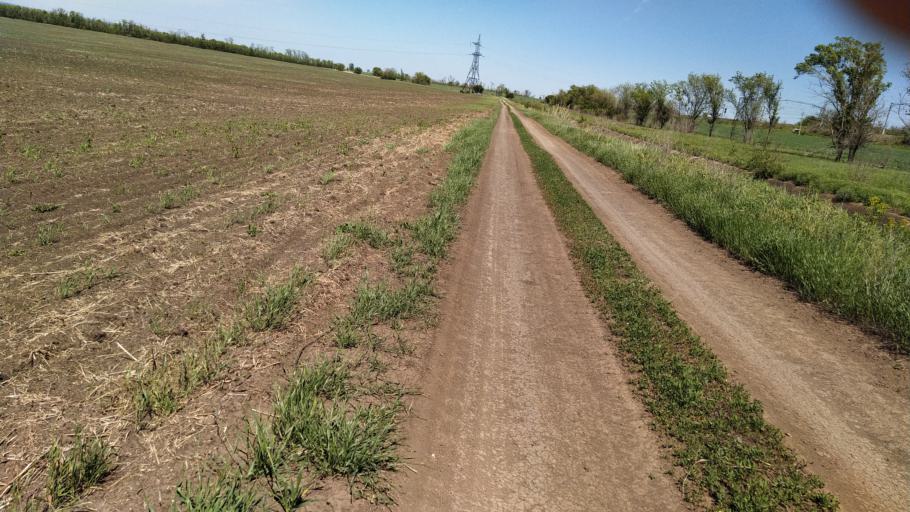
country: RU
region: Rostov
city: Kuleshovka
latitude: 47.0374
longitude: 39.6402
